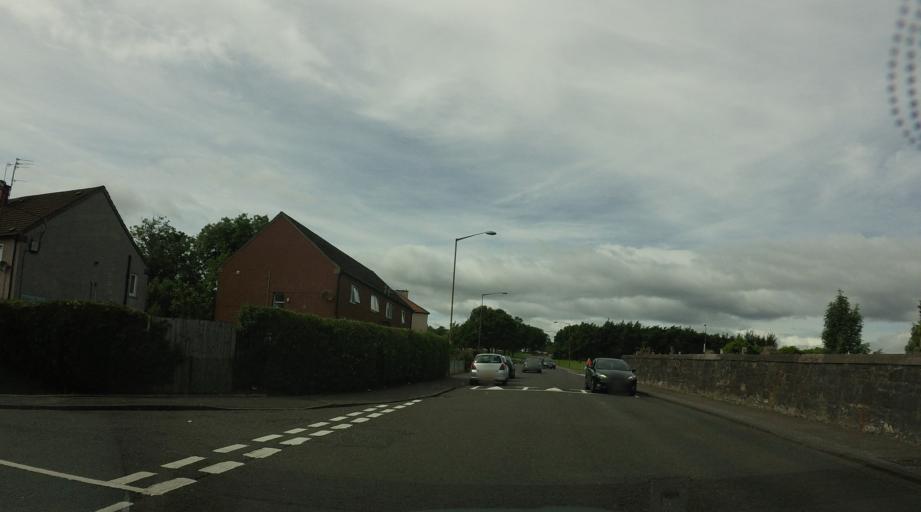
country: GB
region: Scotland
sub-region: West Lothian
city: Broxburn
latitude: 55.9325
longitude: -3.4988
